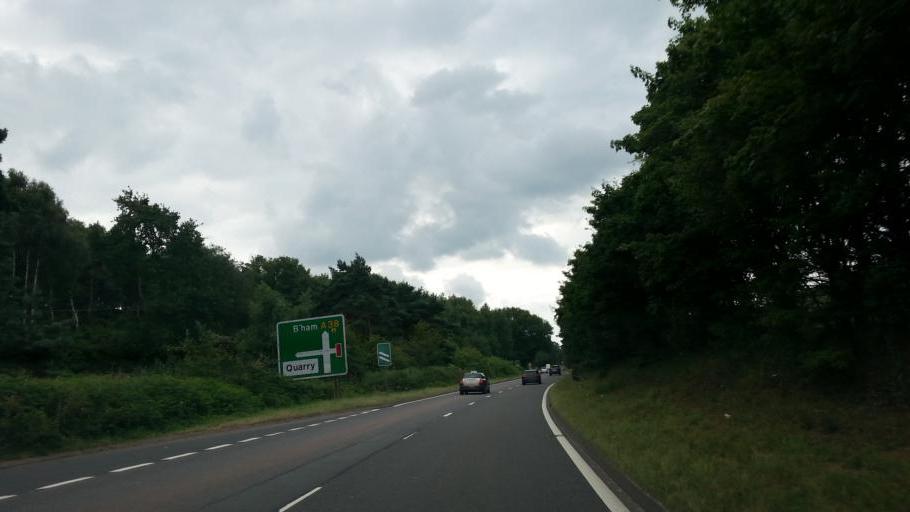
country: GB
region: England
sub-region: Staffordshire
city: Shenstone
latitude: 52.6231
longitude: -1.7980
